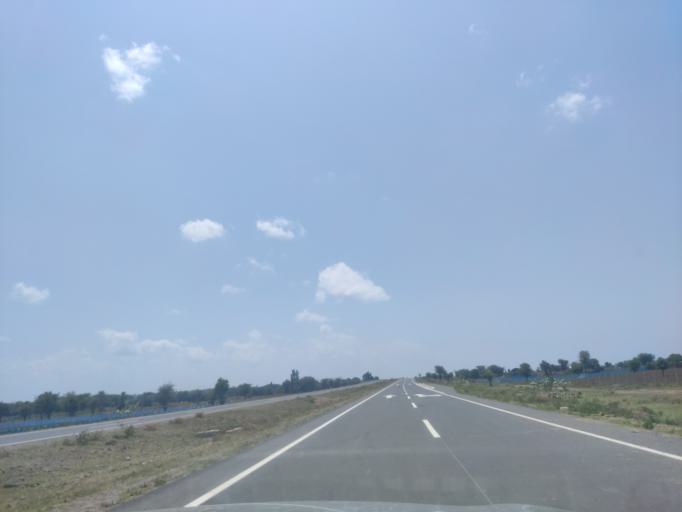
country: ET
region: Oromiya
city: Mojo
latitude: 8.3416
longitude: 38.9730
